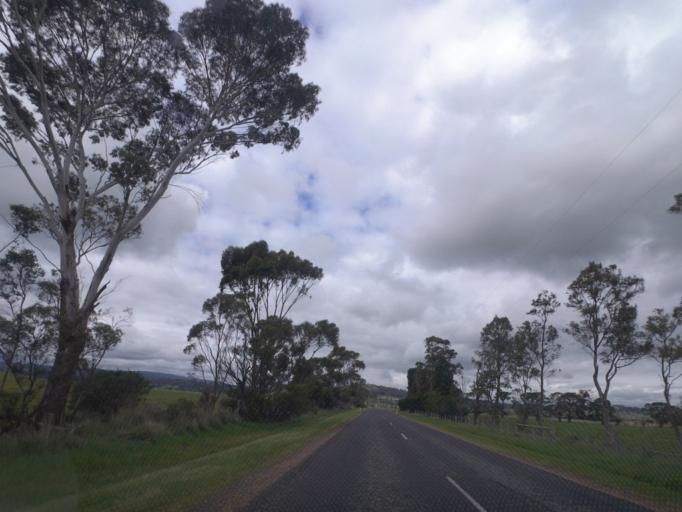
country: AU
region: Victoria
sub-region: Whittlesea
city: Whittlesea
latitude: -37.4732
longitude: 145.0131
